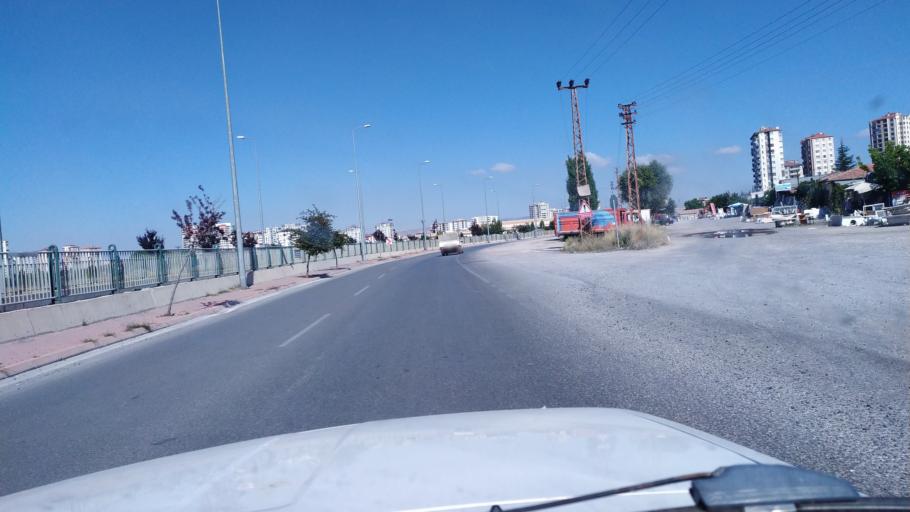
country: TR
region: Kayseri
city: Talas
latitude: 38.7347
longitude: 35.5469
